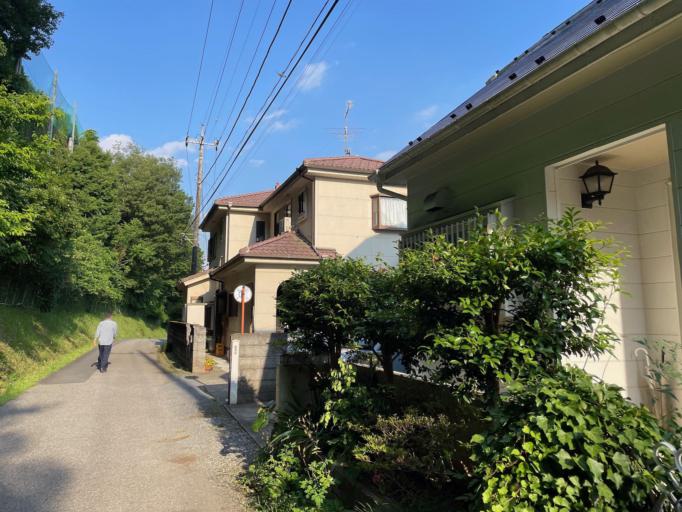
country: JP
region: Saitama
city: Sakado
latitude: 36.0045
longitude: 139.3747
